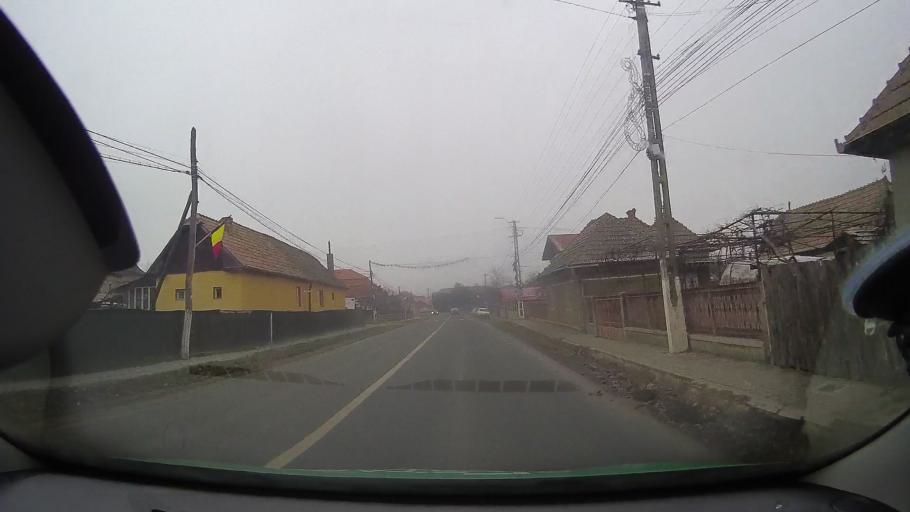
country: RO
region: Cluj
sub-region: Comuna Mihai Viteazu
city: Mihai Viteazu
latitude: 46.5408
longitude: 23.7554
